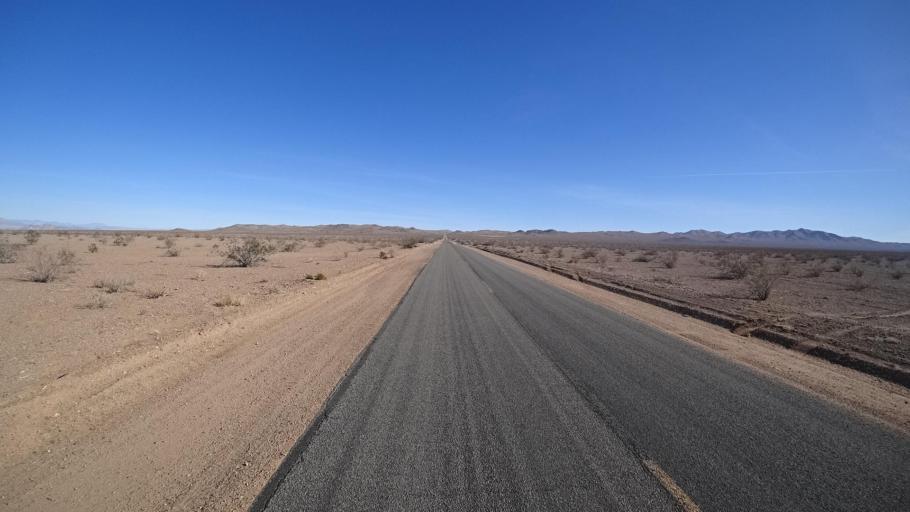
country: US
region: California
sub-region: Kern County
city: China Lake Acres
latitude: 35.5584
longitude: -117.7565
